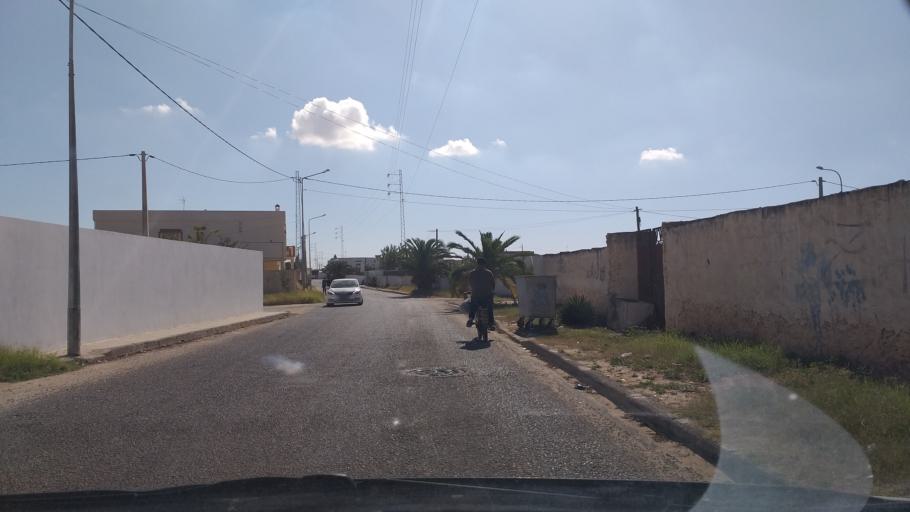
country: TN
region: Safaqis
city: Al Qarmadah
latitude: 34.8031
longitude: 10.7708
